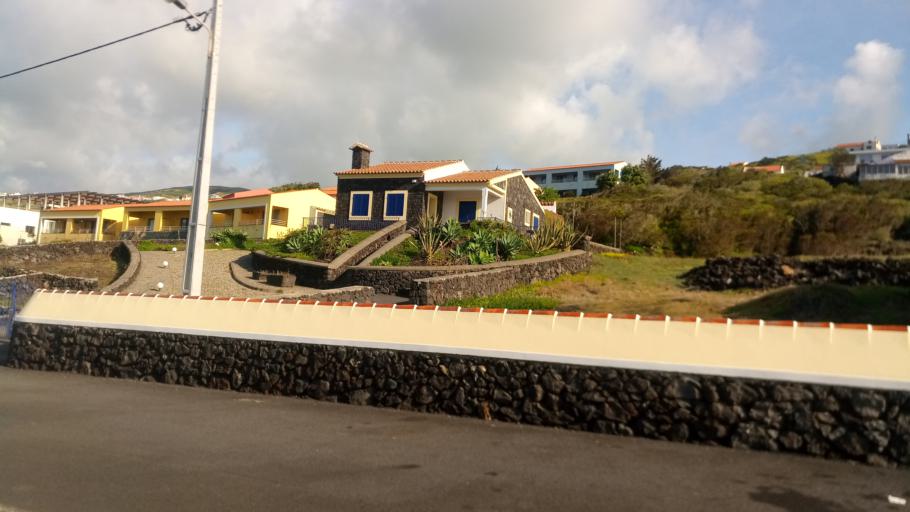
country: PT
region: Azores
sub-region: Angra do Heroismo
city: Angra do Heroismo
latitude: 38.6479
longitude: -27.1536
